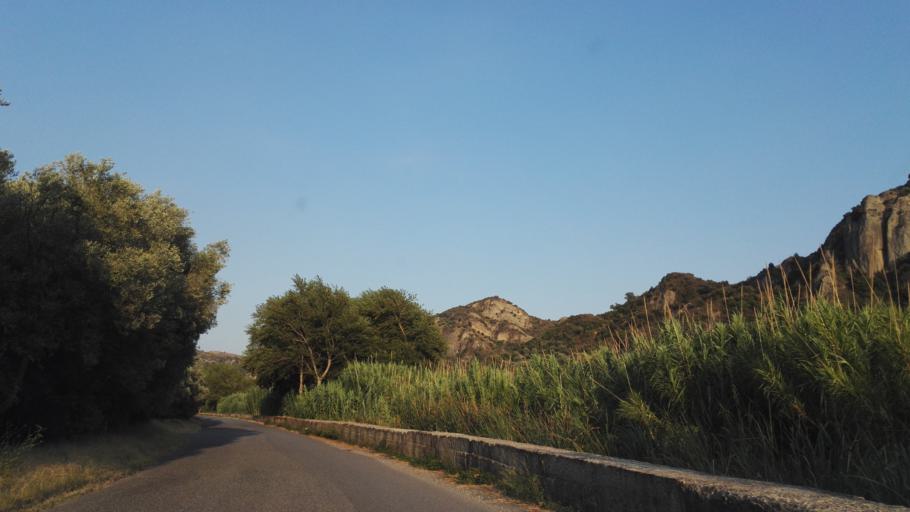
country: IT
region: Calabria
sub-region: Provincia di Reggio Calabria
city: Caulonia
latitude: 38.4032
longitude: 16.3940
